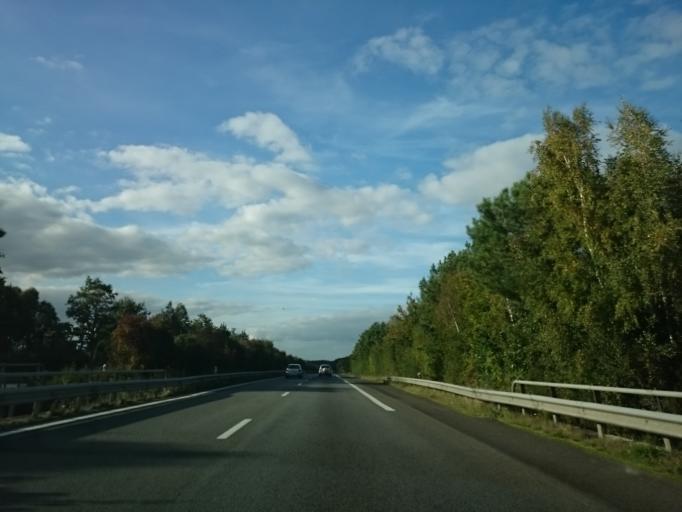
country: FR
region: Pays de la Loire
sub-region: Departement de la Loire-Atlantique
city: Derval
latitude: 47.6363
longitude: -1.6513
